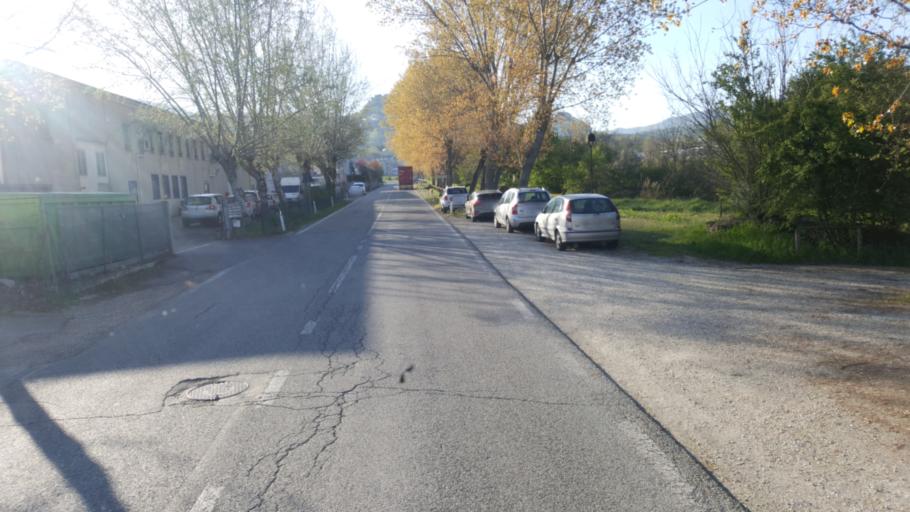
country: SM
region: Acquaviva
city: Acquaviva
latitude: 43.9409
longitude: 12.4081
